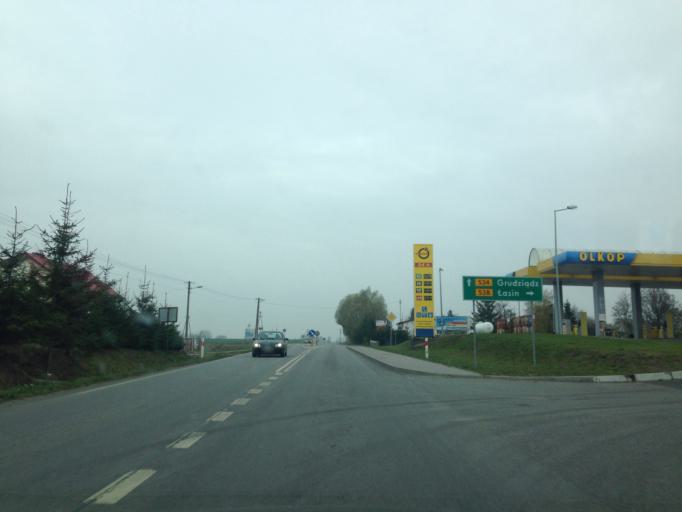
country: PL
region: Kujawsko-Pomorskie
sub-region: Powiat grudziadzki
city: Radzyn Chelminski
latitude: 53.3954
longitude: 18.9318
